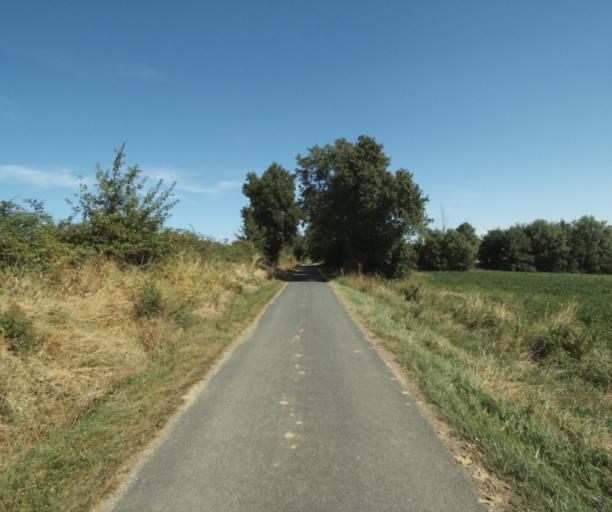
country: FR
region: Midi-Pyrenees
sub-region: Departement de la Haute-Garonne
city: Auriac-sur-Vendinelle
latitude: 43.5229
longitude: 1.8870
